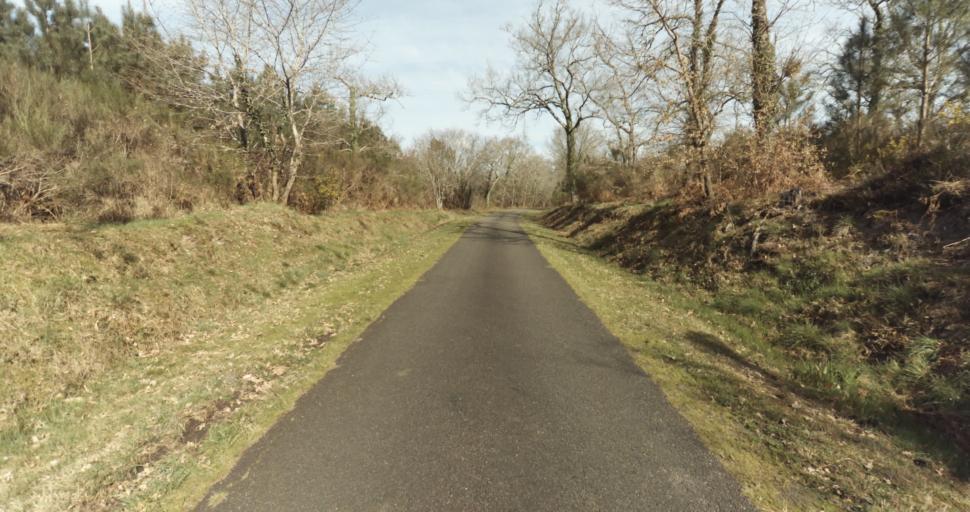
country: FR
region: Aquitaine
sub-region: Departement des Landes
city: Roquefort
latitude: 44.0695
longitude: -0.3572
